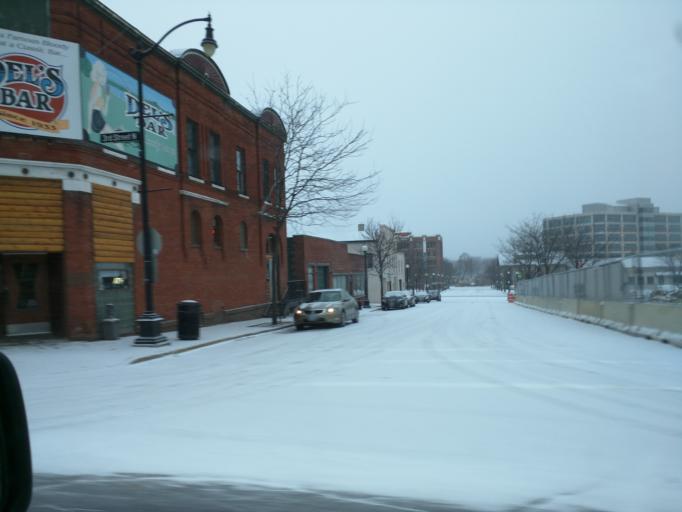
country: US
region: Wisconsin
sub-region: La Crosse County
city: La Crosse
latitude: 43.8147
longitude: -91.2512
